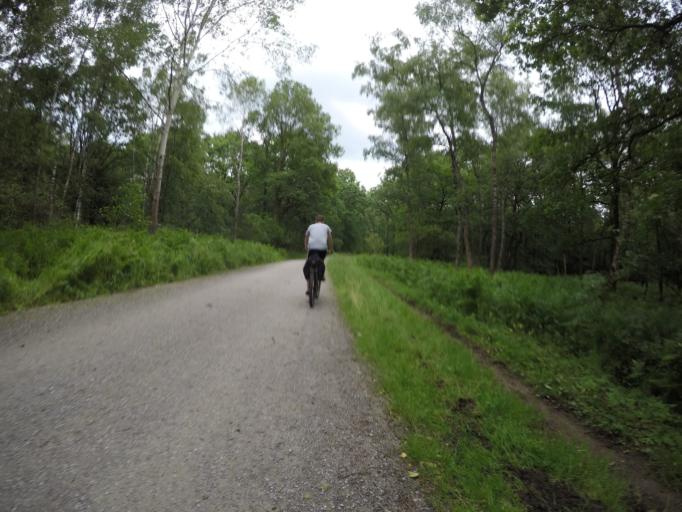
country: DE
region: North Rhine-Westphalia
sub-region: Regierungsbezirk Dusseldorf
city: Schermbeck
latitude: 51.5935
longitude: 6.8596
